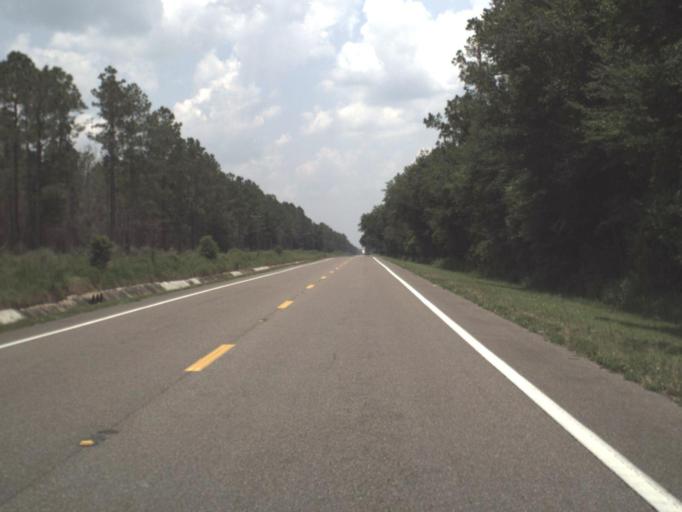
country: US
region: Florida
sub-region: Putnam County
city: Palatka
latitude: 29.4963
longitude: -81.7453
